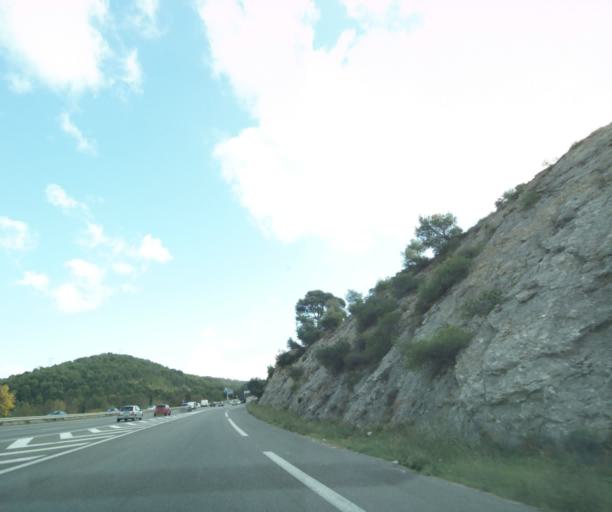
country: FR
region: Provence-Alpes-Cote d'Azur
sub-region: Departement des Bouches-du-Rhone
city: Les Pennes-Mirabeau
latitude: 43.4061
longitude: 5.3351
